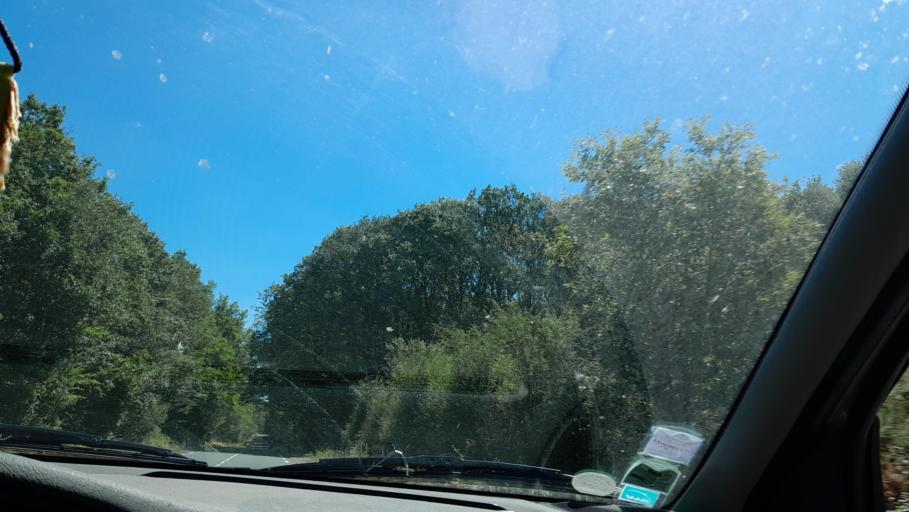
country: FR
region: Pays de la Loire
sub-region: Departement de Maine-et-Loire
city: Pouance
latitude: 47.6934
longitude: -1.1851
